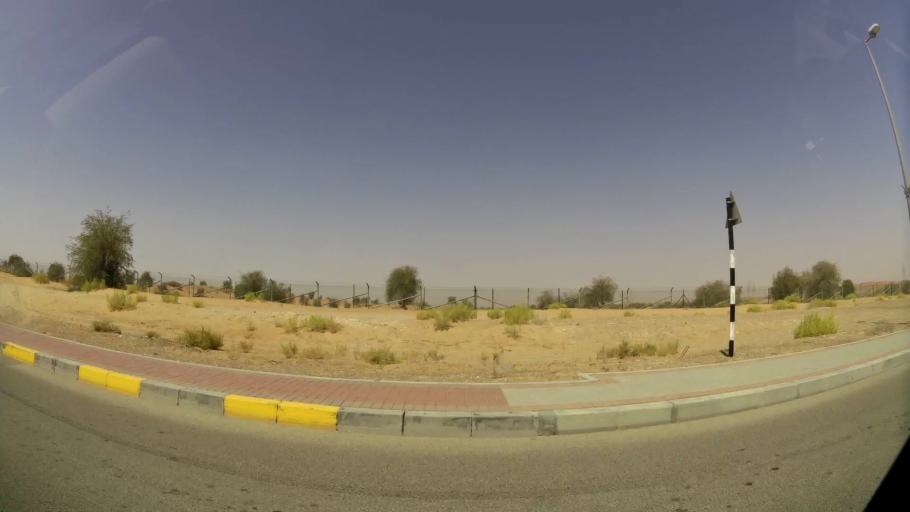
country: OM
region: Al Buraimi
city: Al Buraymi
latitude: 24.3014
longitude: 55.7488
